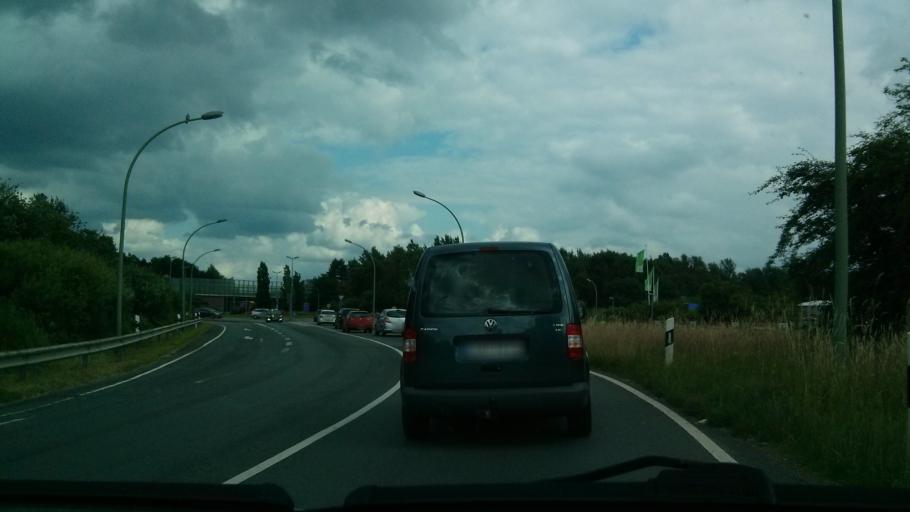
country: DE
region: Lower Saxony
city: Schiffdorf
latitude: 53.5262
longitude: 8.6197
